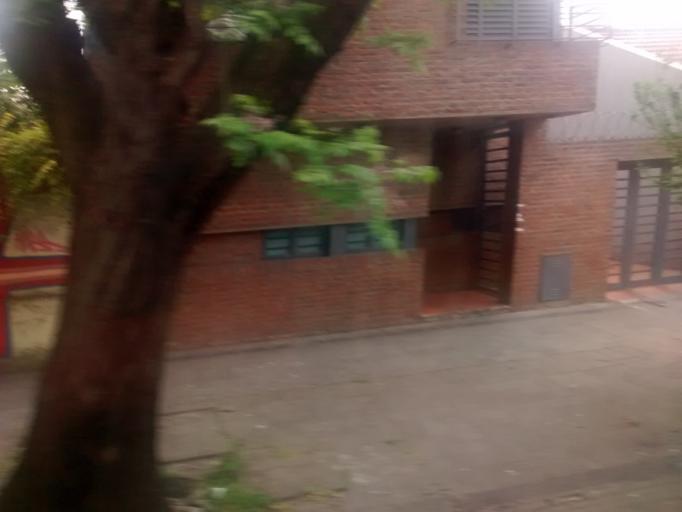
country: AR
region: Buenos Aires
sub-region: Partido de La Plata
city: La Plata
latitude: -34.9320
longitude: -57.9353
